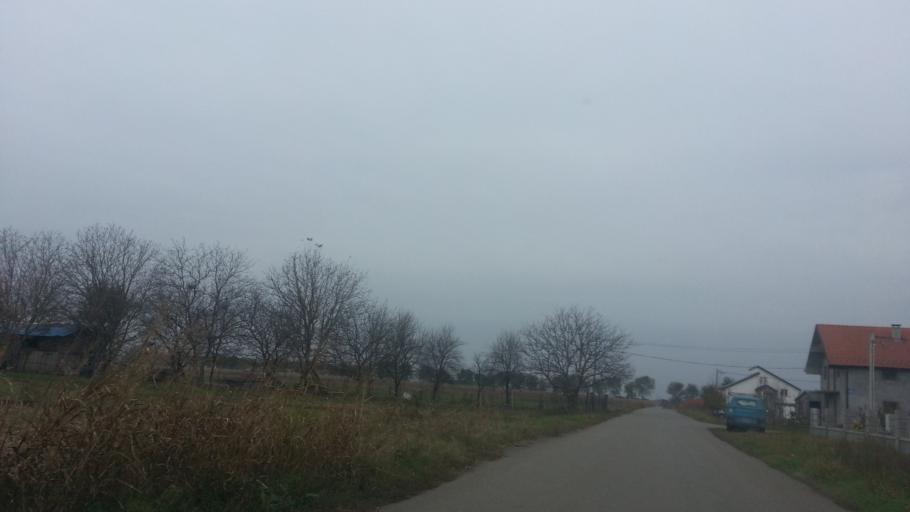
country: RS
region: Autonomna Pokrajina Vojvodina
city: Nova Pazova
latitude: 44.9553
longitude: 20.2069
